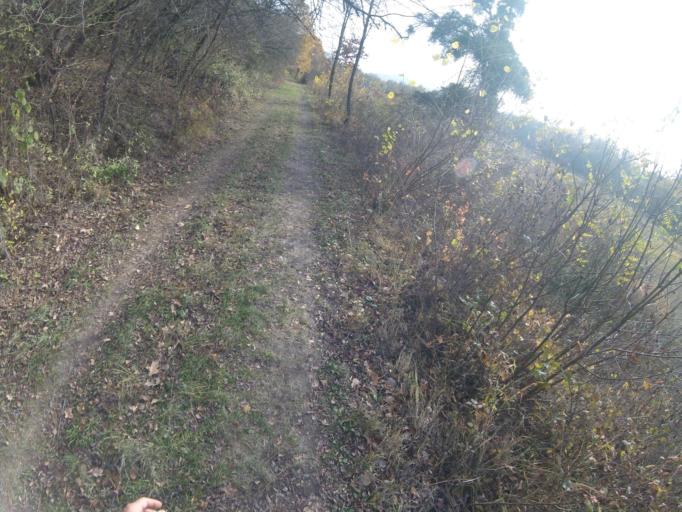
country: HU
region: Borsod-Abauj-Zemplen
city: Gonc
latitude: 48.5029
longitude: 21.4514
